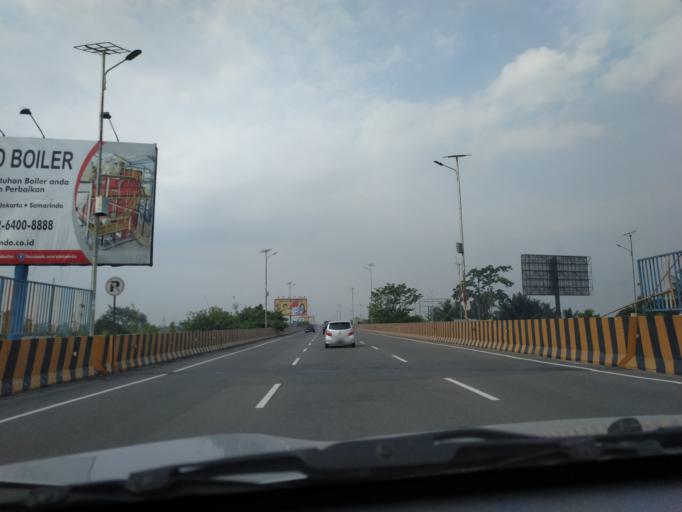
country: ID
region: North Sumatra
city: Percut
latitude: 3.6088
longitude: 98.8528
